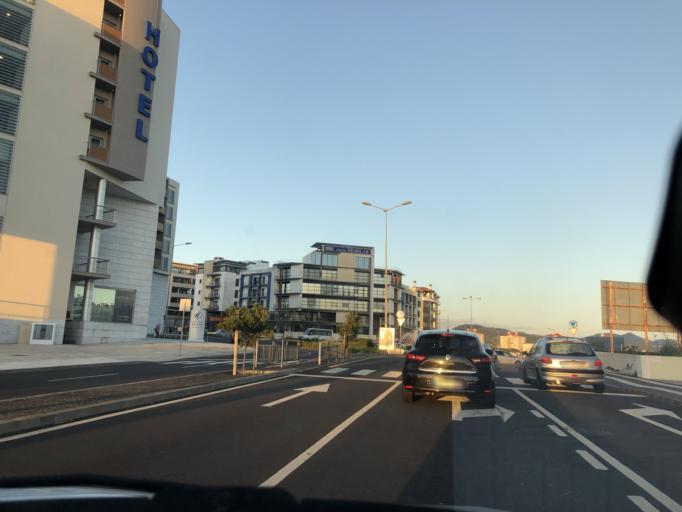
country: PT
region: Azores
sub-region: Ponta Delgada
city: Rosto de Cao
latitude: 37.7503
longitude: -25.6589
